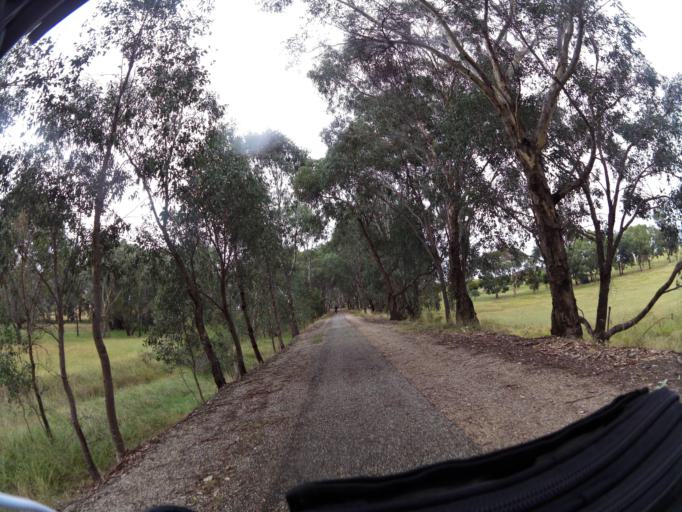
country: AU
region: New South Wales
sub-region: Albury Municipality
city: East Albury
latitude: -36.2234
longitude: 147.1129
